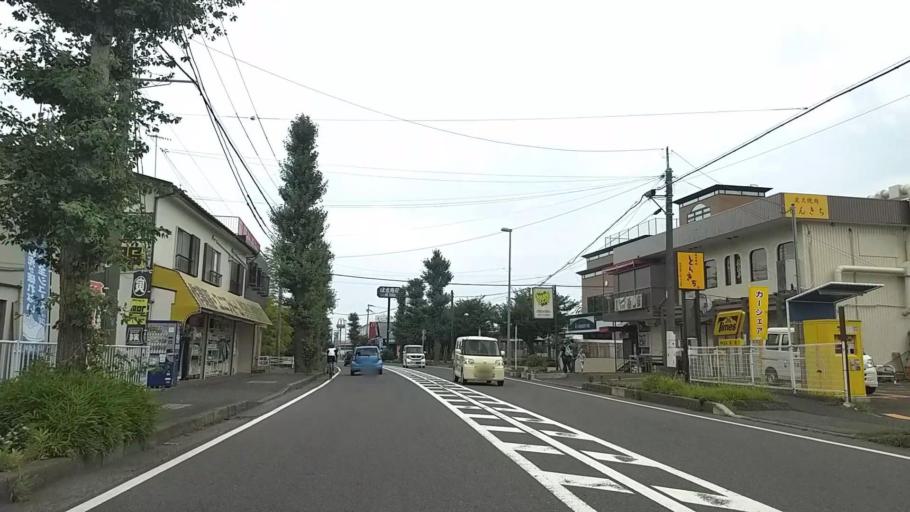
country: JP
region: Kanagawa
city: Minami-rinkan
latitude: 35.4644
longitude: 139.4305
